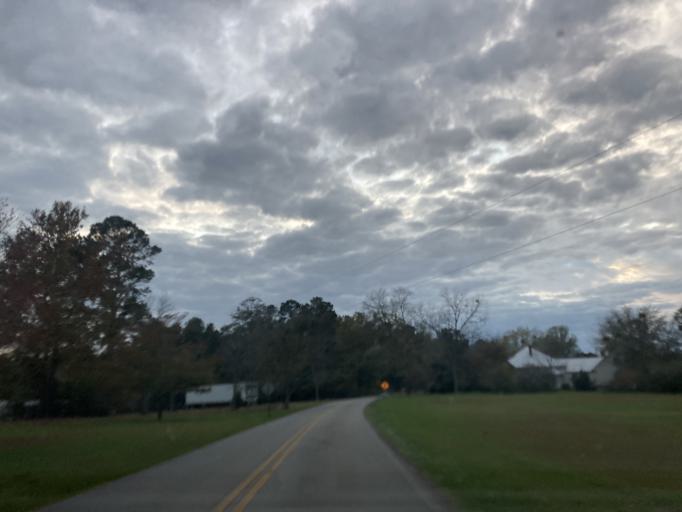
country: US
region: Georgia
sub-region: Jones County
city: Gray
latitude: 32.9776
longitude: -83.5124
